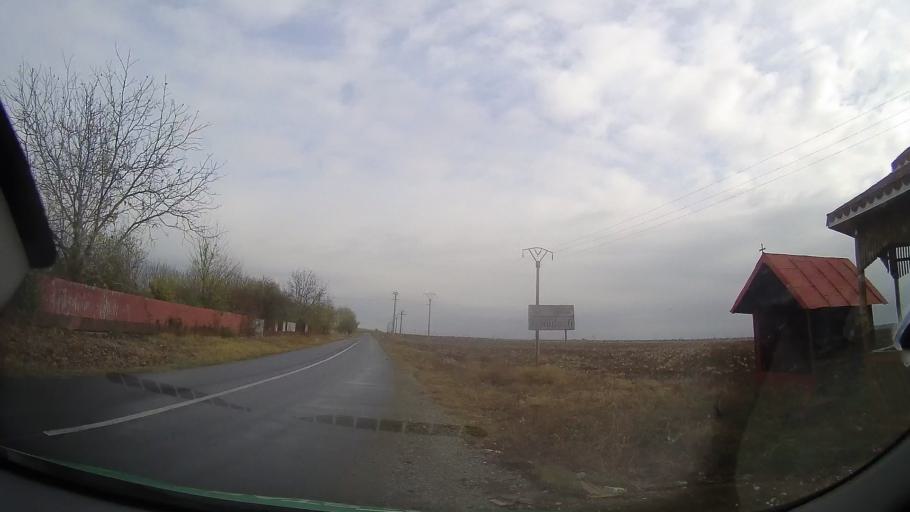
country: RO
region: Ialomita
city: Brazii
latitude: 44.7571
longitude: 26.3704
